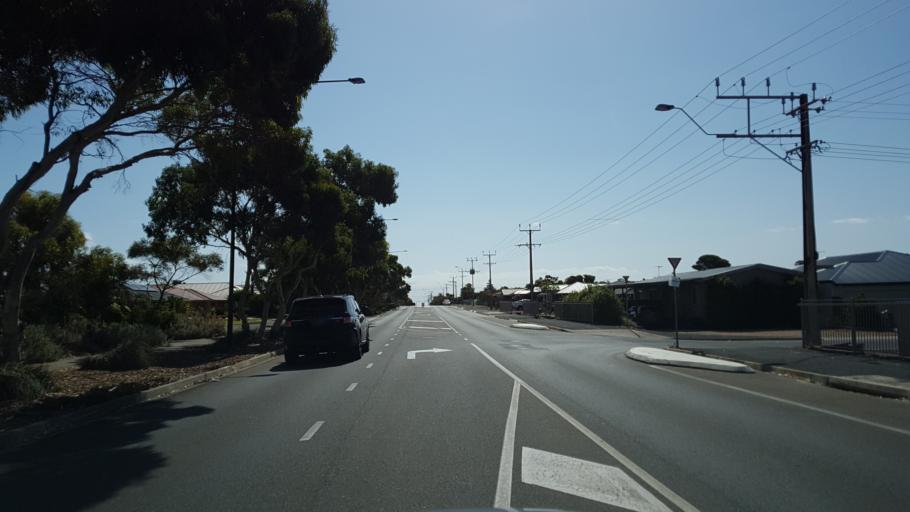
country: AU
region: South Australia
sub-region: Onkaparinga
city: Port Willunga
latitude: -35.2790
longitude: 138.4504
